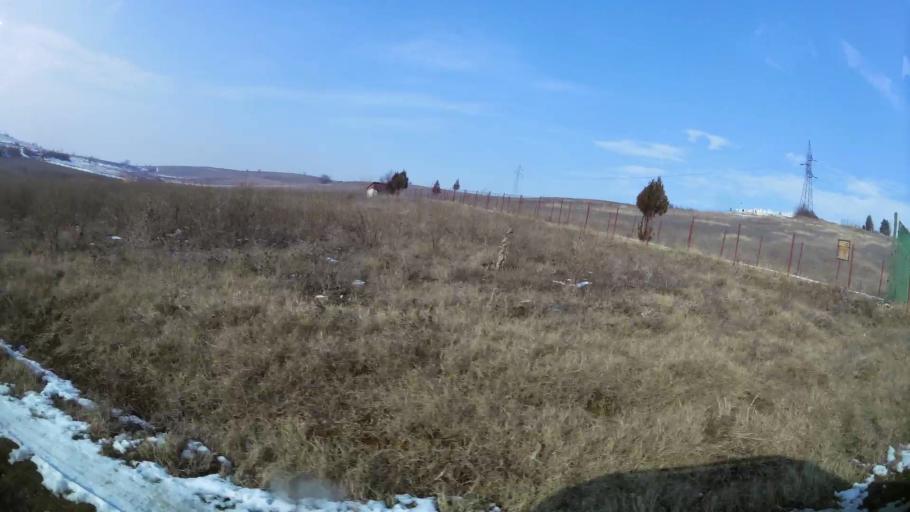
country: MK
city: Creshevo
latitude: 42.0156
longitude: 21.4916
